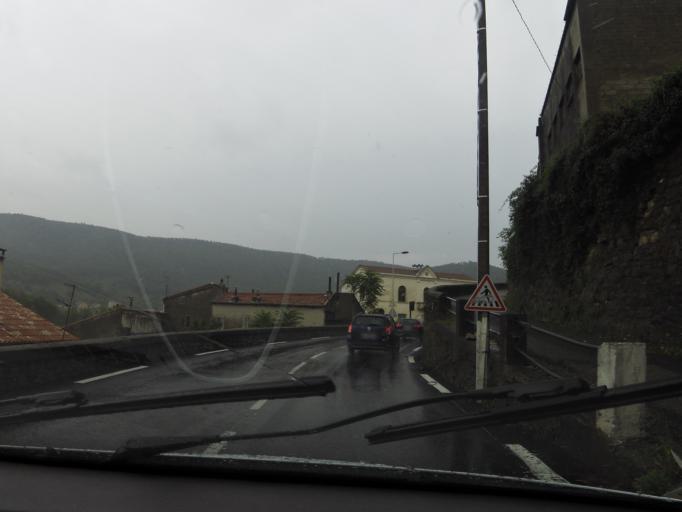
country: FR
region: Languedoc-Roussillon
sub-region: Departement du Gard
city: Les Salles-du-Gardon
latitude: 44.2072
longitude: 4.0330
